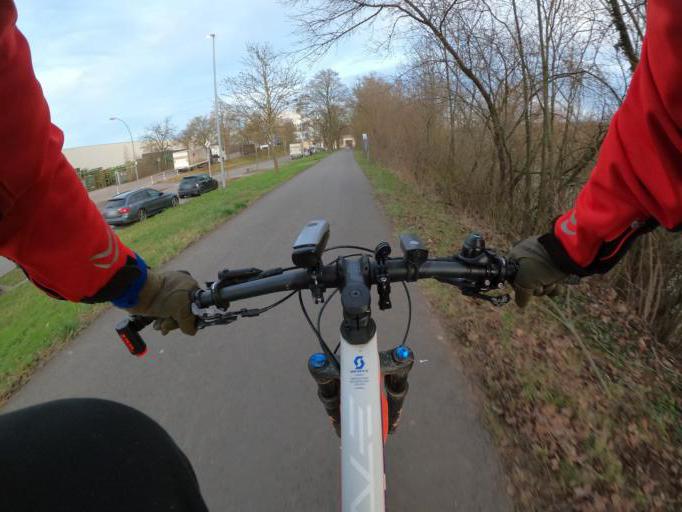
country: DE
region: Baden-Wuerttemberg
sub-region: Regierungsbezirk Stuttgart
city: Denkendorf
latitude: 48.7228
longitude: 9.3408
